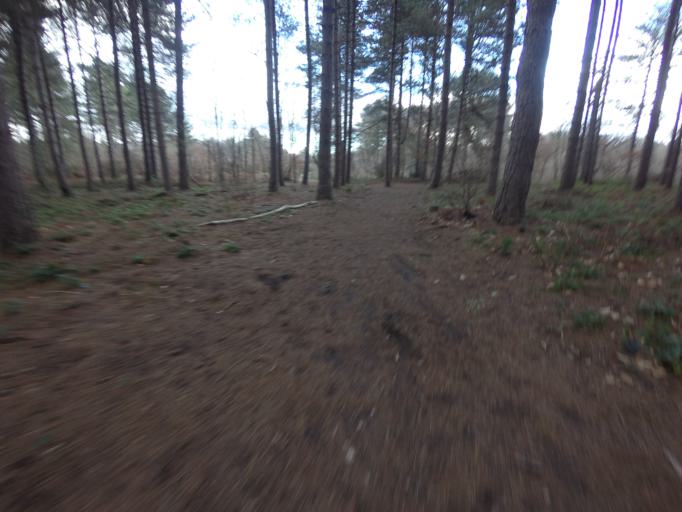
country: GB
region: England
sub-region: Greater London
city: Bexley
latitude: 51.4211
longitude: 0.1567
